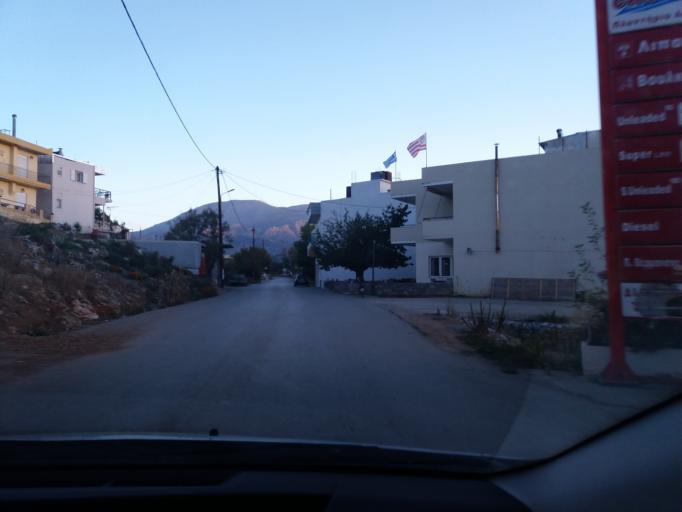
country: GR
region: Crete
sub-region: Nomos Irakleiou
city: Malia
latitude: 35.1960
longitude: 25.4891
